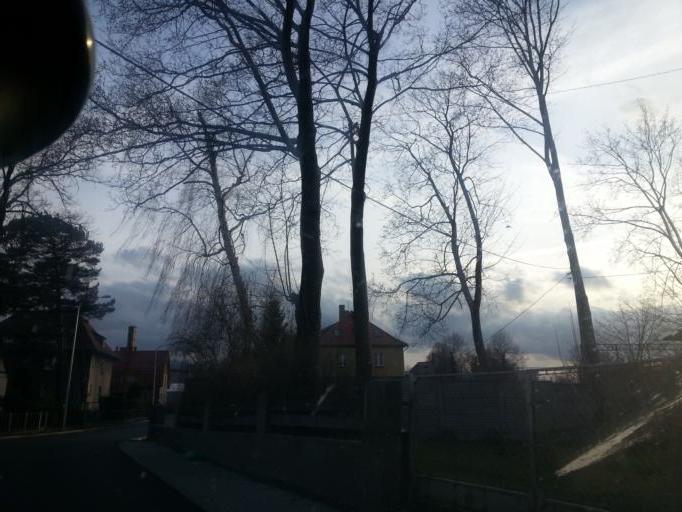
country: PL
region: Lower Silesian Voivodeship
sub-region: Jelenia Gora
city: Cieplice Slaskie Zdroj
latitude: 50.8712
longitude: 15.6937
